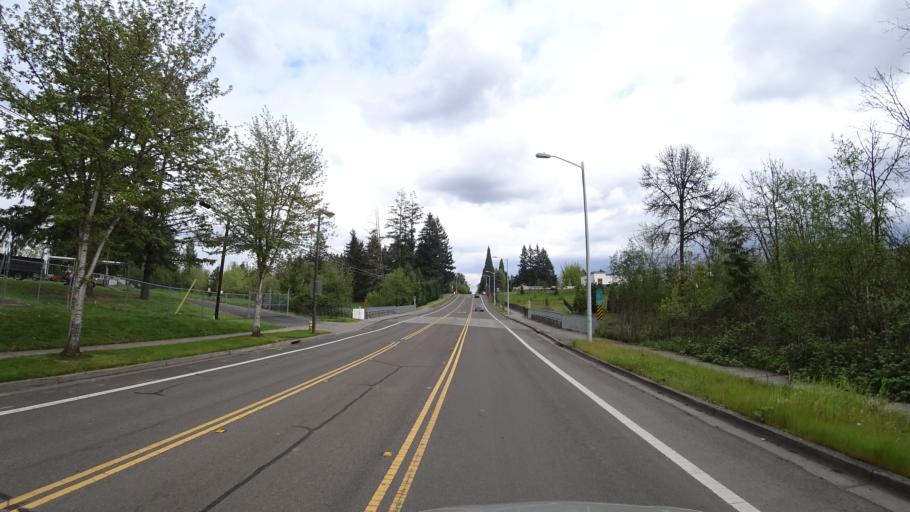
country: US
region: Oregon
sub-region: Washington County
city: Hillsboro
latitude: 45.5382
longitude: -122.9364
